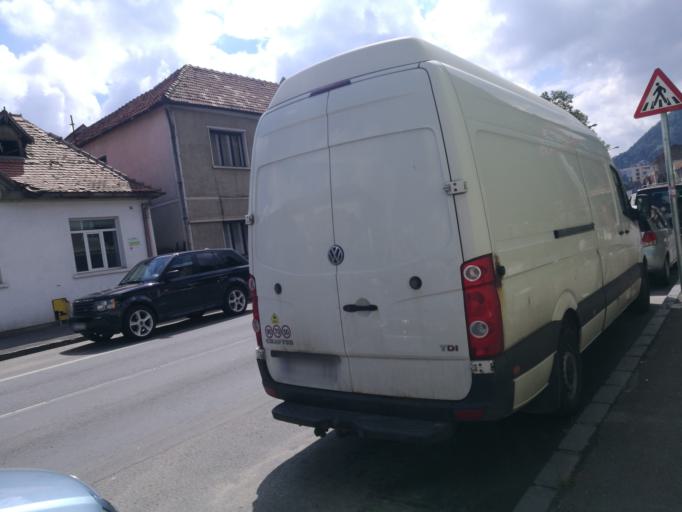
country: RO
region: Brasov
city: Brasov
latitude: 45.6520
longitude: 25.5951
